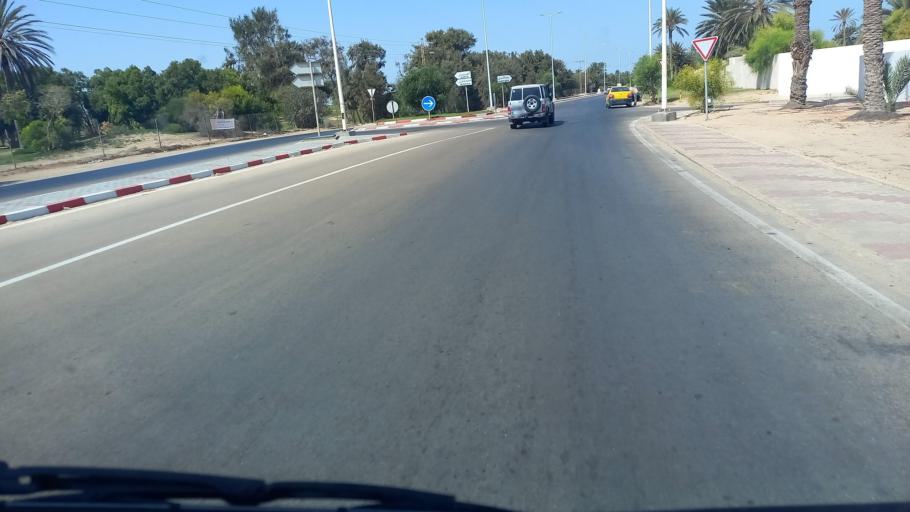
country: TN
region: Madanin
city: Midoun
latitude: 33.8252
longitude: 11.0225
